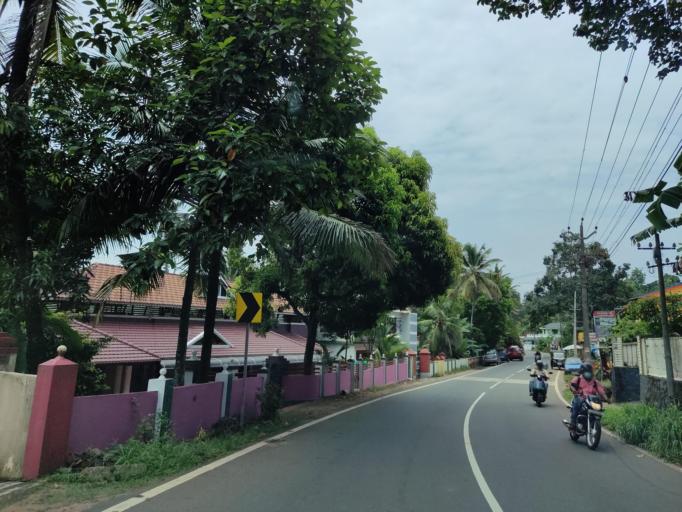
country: IN
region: Kerala
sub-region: Alappuzha
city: Chengannur
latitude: 9.2860
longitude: 76.6135
